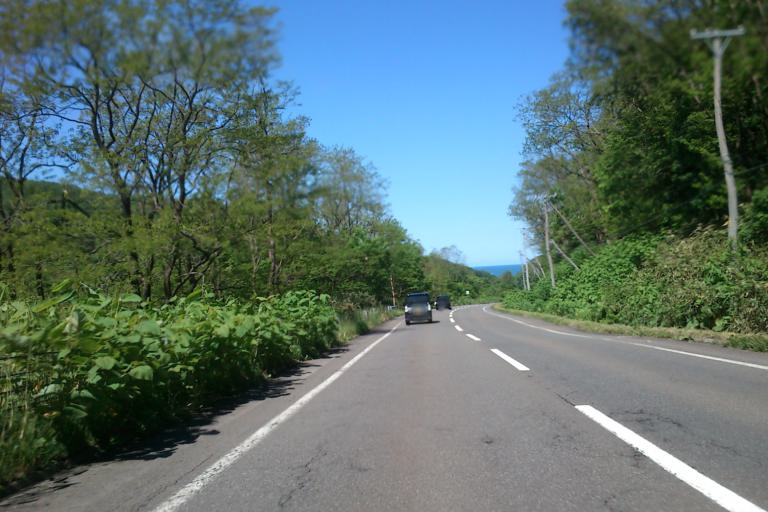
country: JP
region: Hokkaido
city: Ishikari
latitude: 43.5552
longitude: 141.3995
